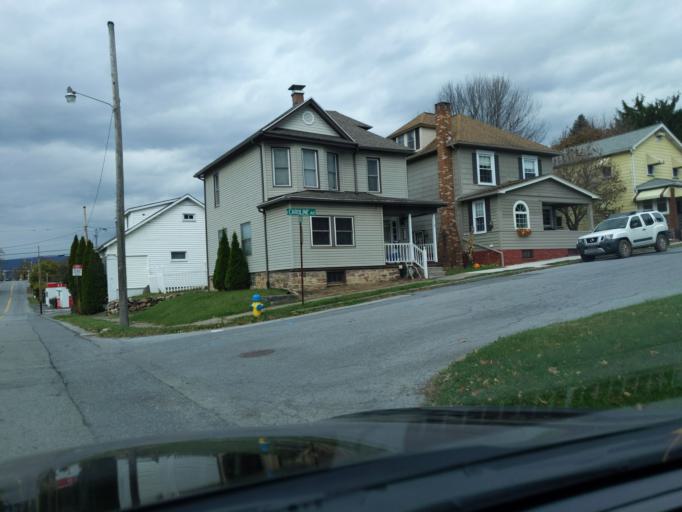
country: US
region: Pennsylvania
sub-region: Blair County
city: Altoona
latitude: 40.5189
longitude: -78.3742
